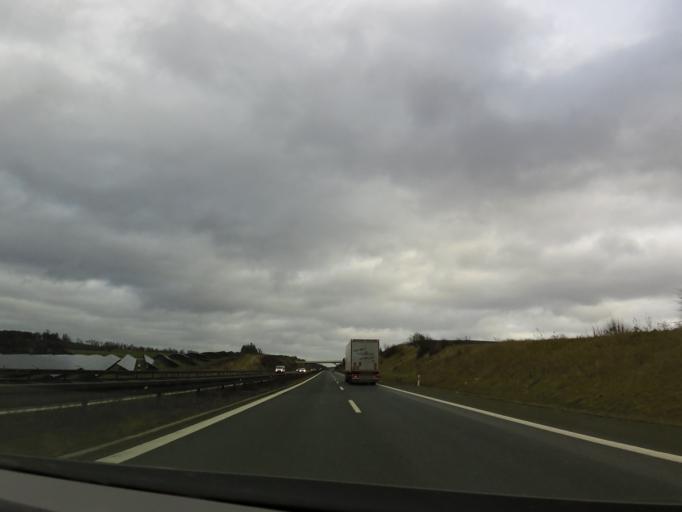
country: DE
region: Bavaria
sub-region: Upper Franconia
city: Gattendorf
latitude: 50.3482
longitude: 11.9804
